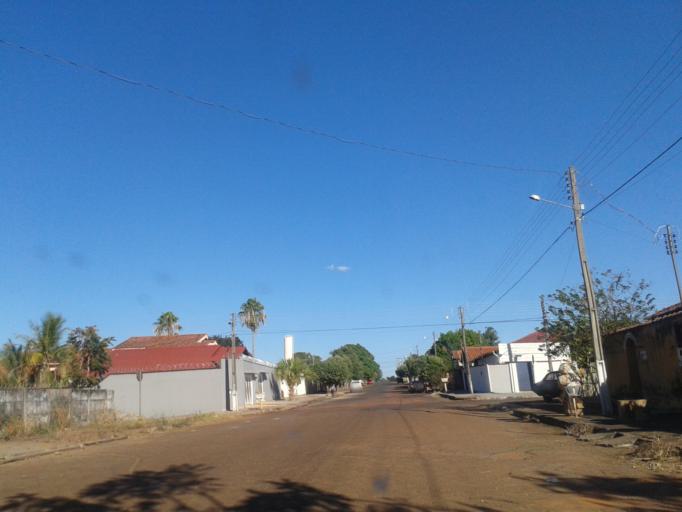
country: BR
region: Goias
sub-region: Sao Miguel Do Araguaia
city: Sao Miguel do Araguaia
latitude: -13.2717
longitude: -50.1590
